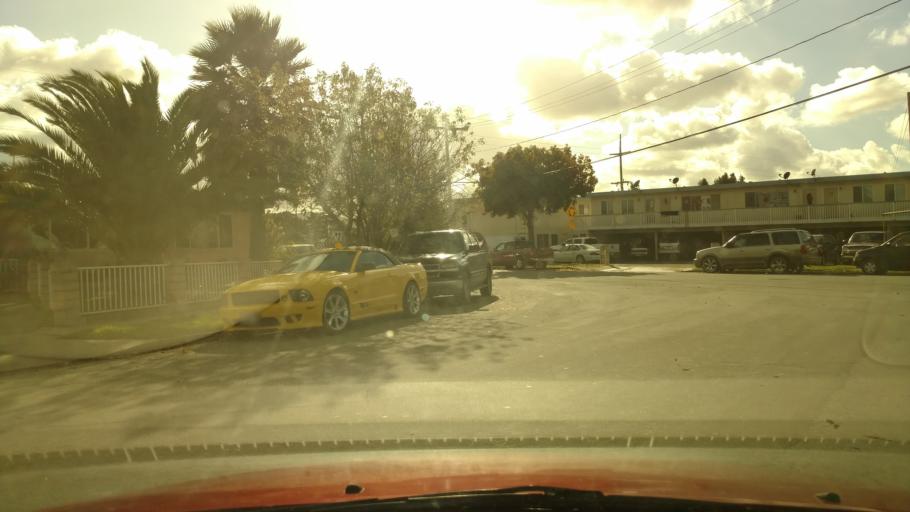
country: US
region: California
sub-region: Monterey County
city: Salinas
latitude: 36.6731
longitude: -121.6175
